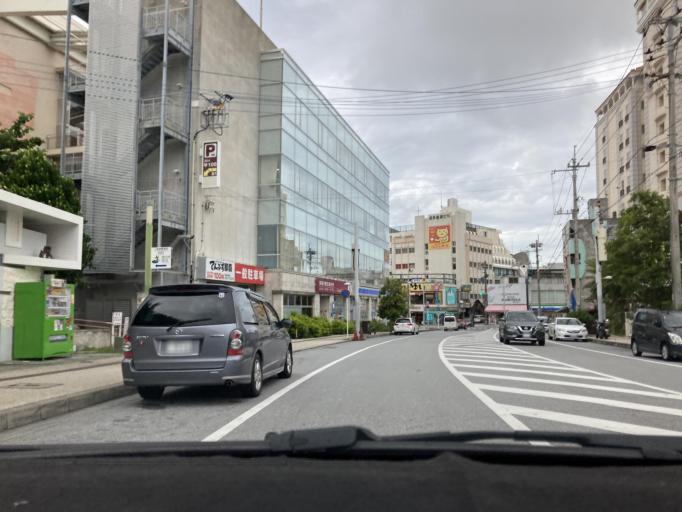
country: JP
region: Okinawa
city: Naha-shi
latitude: 26.2158
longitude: 127.6898
